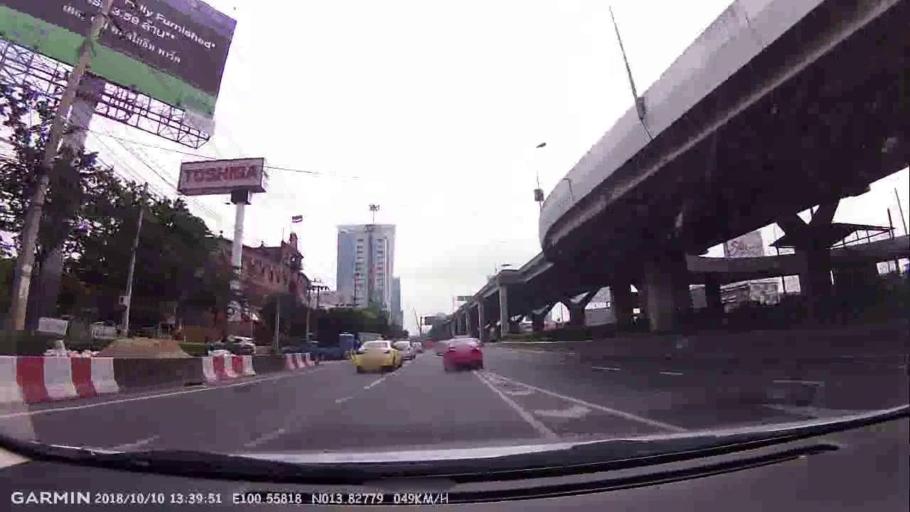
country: TH
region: Bangkok
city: Chatuchak
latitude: 13.8276
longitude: 100.5582
